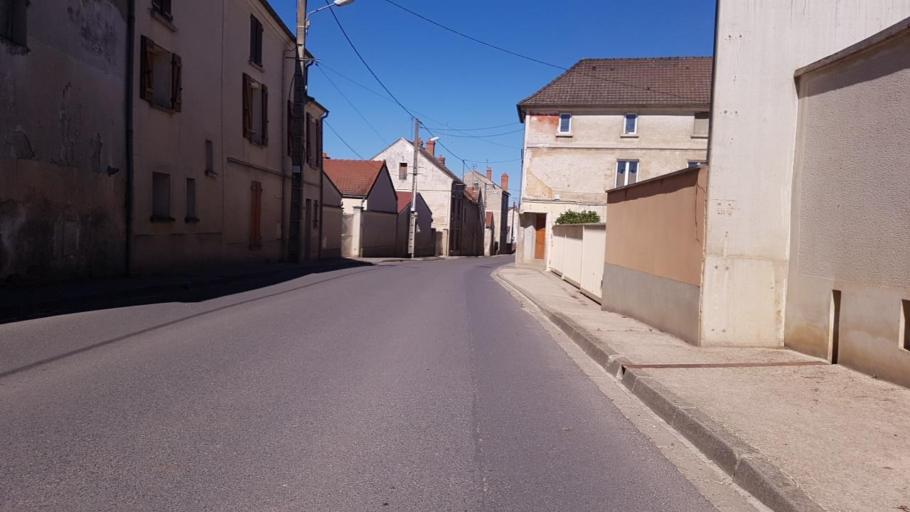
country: FR
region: Picardie
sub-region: Departement de l'Aisne
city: Charly-sur-Marne
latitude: 48.9753
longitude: 3.3040
